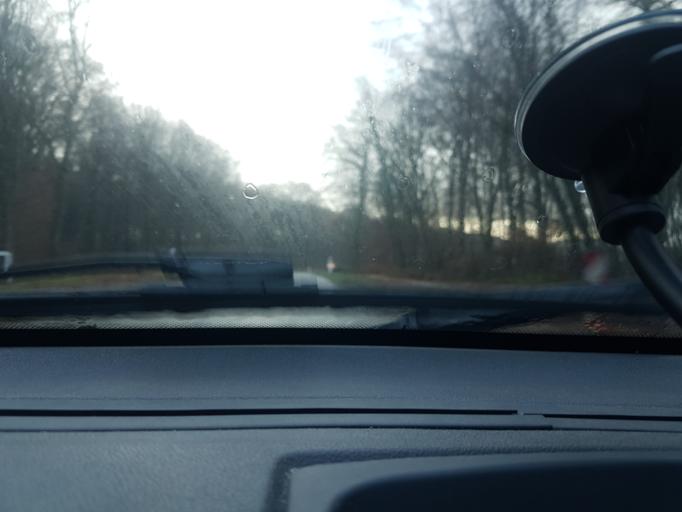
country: FR
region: Franche-Comte
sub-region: Territoire de Belfort
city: Danjoutin
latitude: 47.6092
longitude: 6.8505
